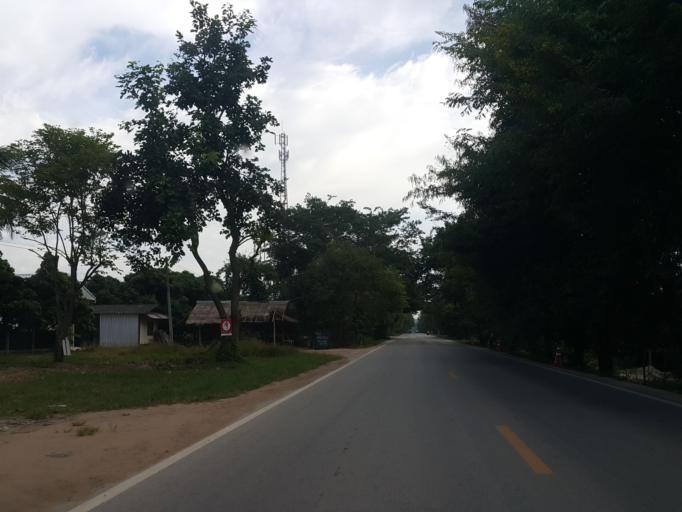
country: TH
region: Chiang Mai
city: Phrao
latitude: 19.2989
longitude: 99.1889
